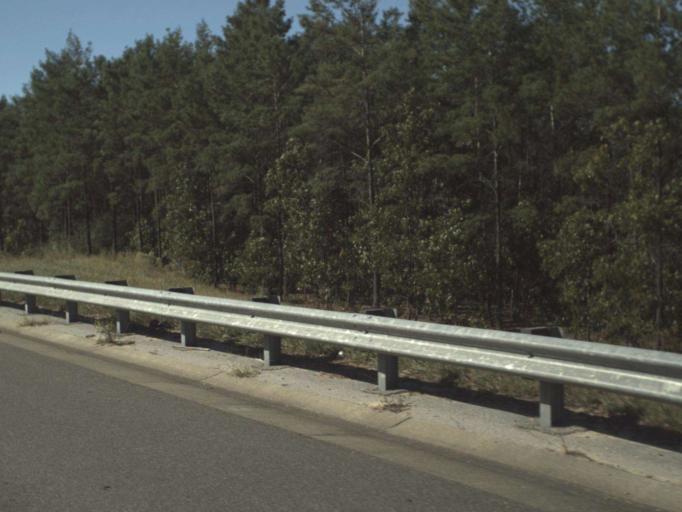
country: US
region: Florida
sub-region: Walton County
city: Freeport
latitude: 30.5099
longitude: -86.1134
